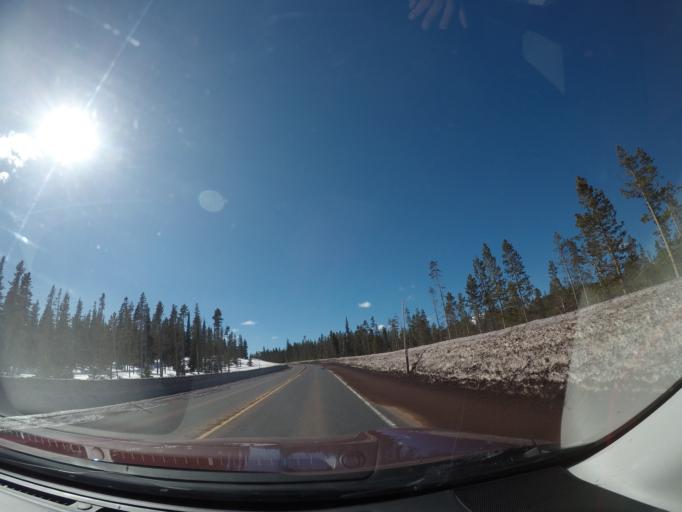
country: US
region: Oregon
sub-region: Deschutes County
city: Sunriver
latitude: 43.9862
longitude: -121.5753
